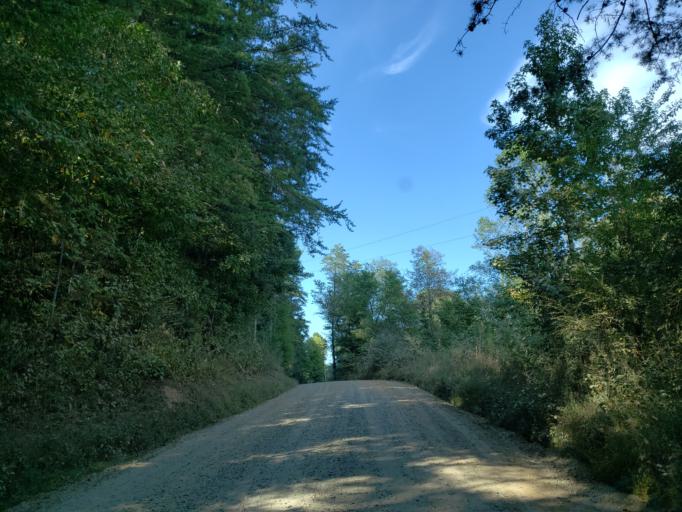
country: US
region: Georgia
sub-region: Gilmer County
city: Ellijay
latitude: 34.5982
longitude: -84.5119
